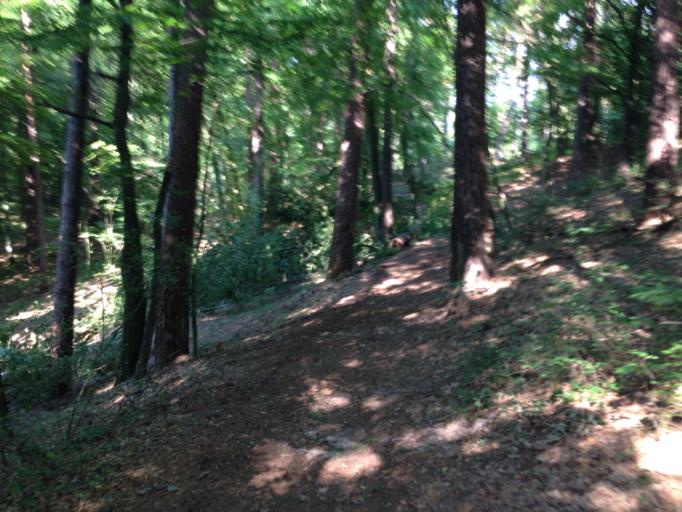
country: PL
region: Kujawsko-Pomorskie
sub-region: Powiat brodnicki
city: Gorzno
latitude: 53.1909
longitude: 19.6538
